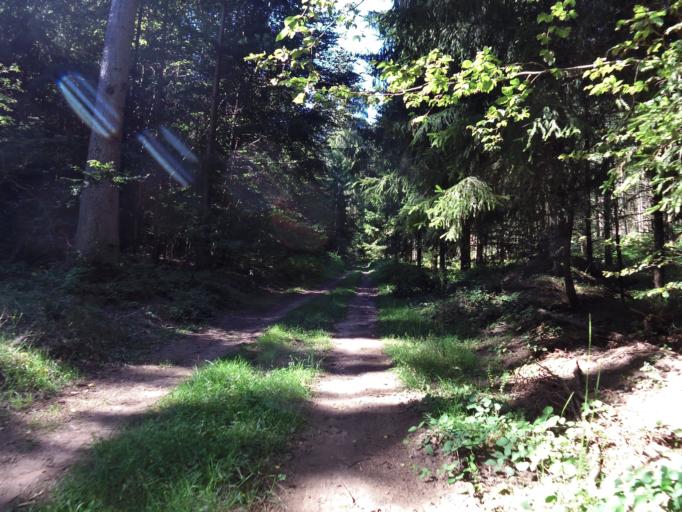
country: DE
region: Rheinland-Pfalz
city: Weidenthal
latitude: 49.4022
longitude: 8.0013
